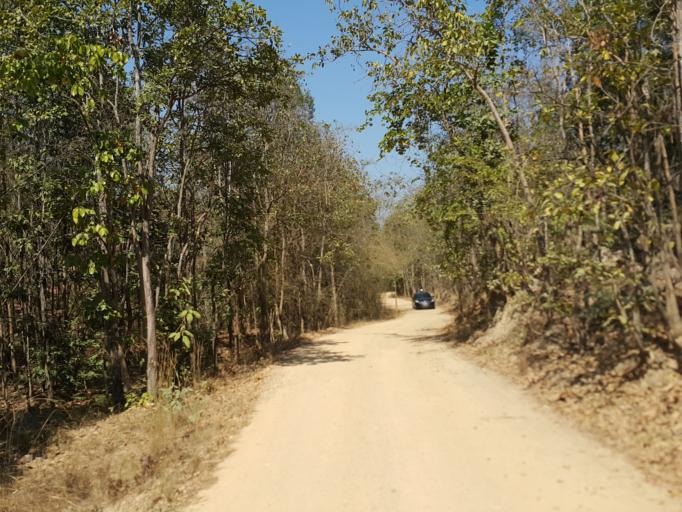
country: TH
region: Chiang Mai
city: Doi Lo
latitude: 18.5214
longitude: 98.7441
